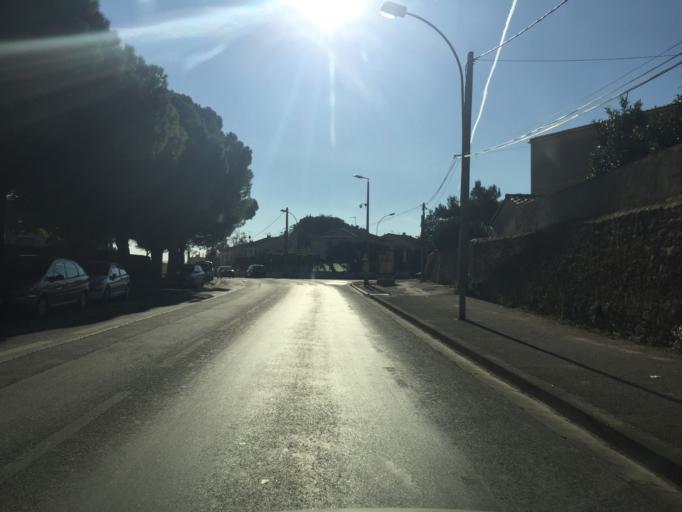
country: FR
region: Provence-Alpes-Cote d'Azur
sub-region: Departement des Bouches-du-Rhone
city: Salon-de-Provence
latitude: 43.6446
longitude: 5.1026
